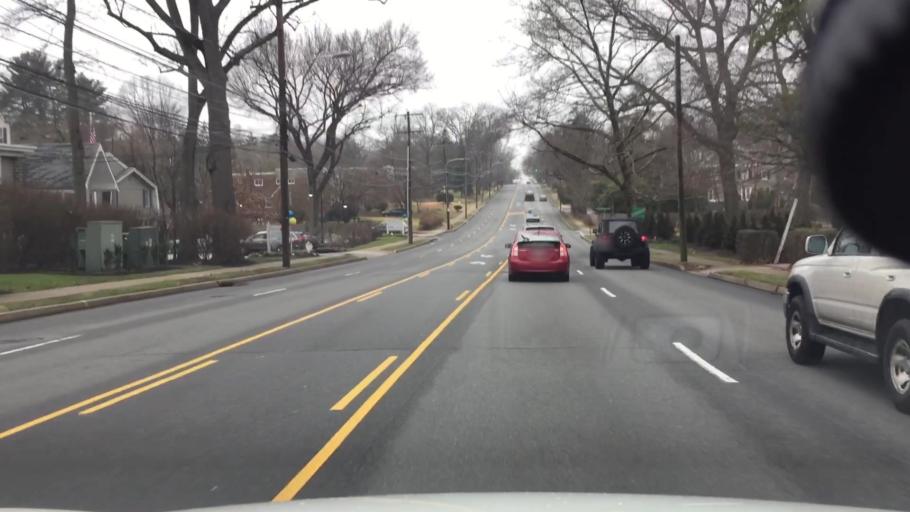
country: US
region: Pennsylvania
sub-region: Montgomery County
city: Wyndmoor
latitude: 40.0775
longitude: -75.1967
